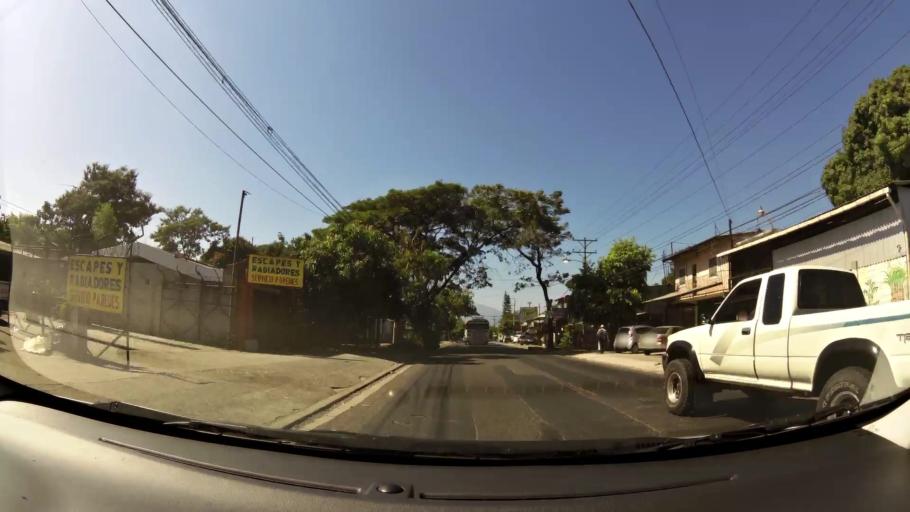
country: SV
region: La Libertad
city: Santa Tecla
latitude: 13.7214
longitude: -89.3646
